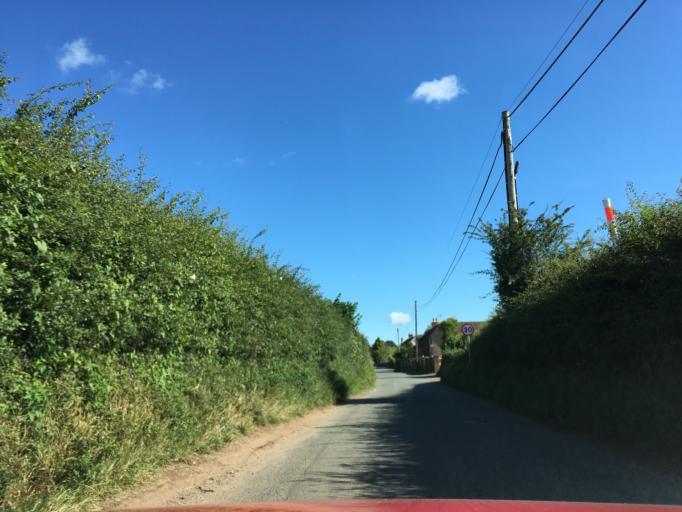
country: GB
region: England
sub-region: Herefordshire
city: Ross on Wye
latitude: 51.9316
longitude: -2.5780
